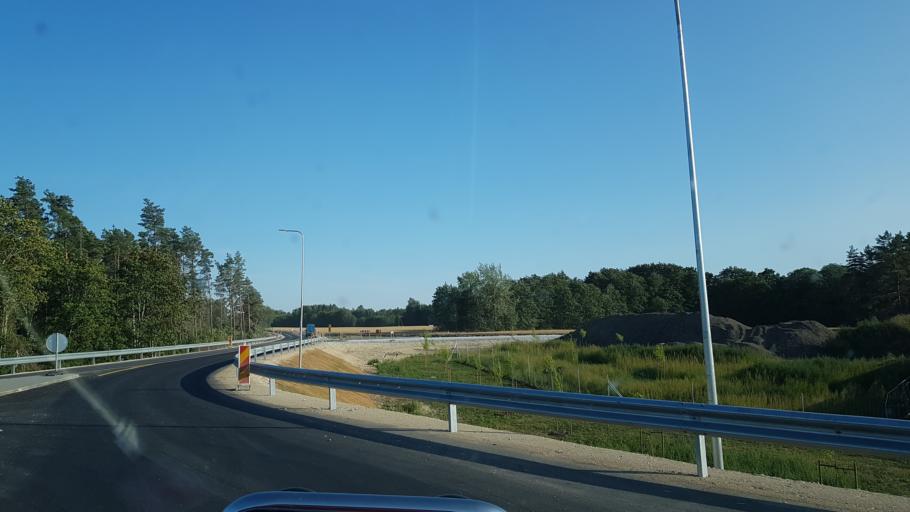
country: EE
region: Harju
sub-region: Raasiku vald
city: Raasiku
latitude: 59.1582
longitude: 25.1897
